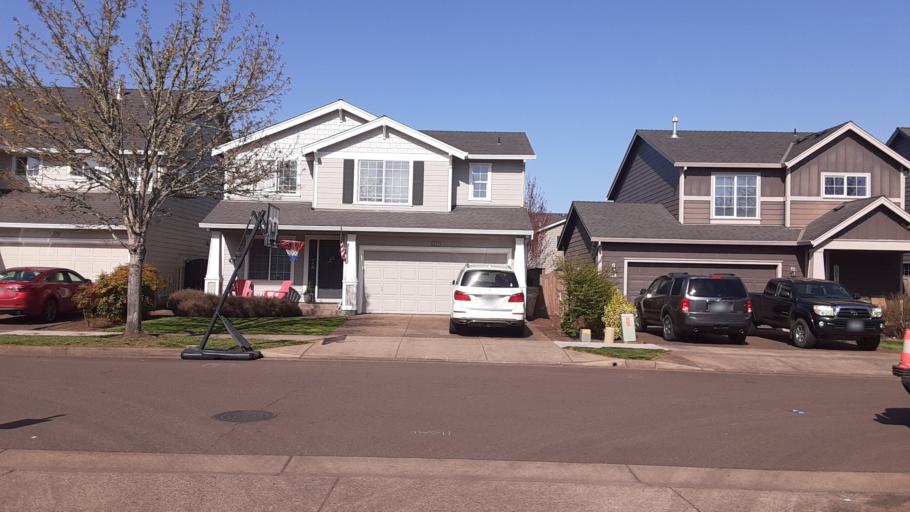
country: US
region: Oregon
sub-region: Benton County
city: Corvallis
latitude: 44.5309
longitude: -123.2562
